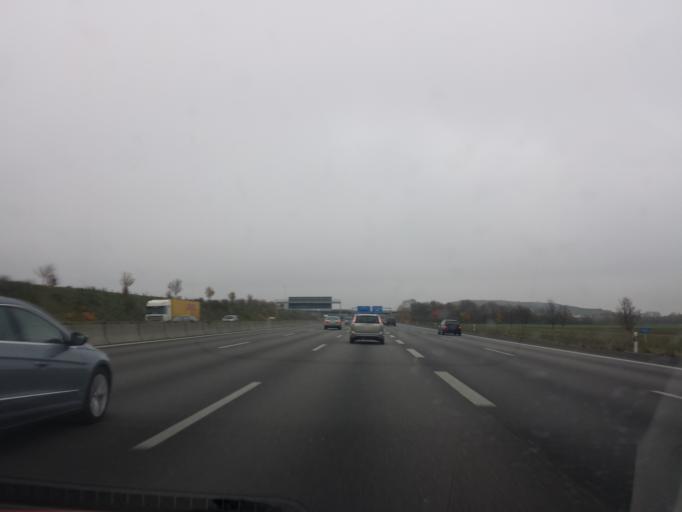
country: DE
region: Bavaria
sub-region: Upper Bavaria
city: Garching bei Munchen
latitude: 48.2372
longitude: 11.6372
